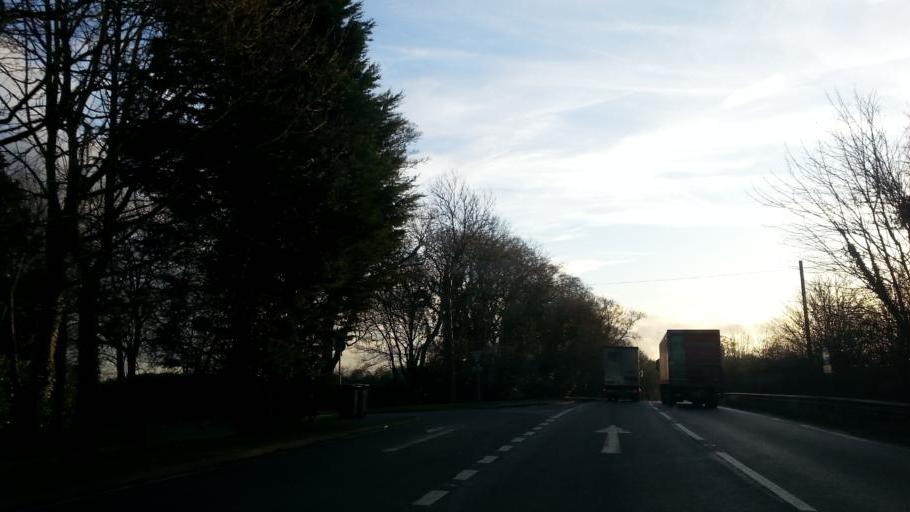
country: GB
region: England
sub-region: Northamptonshire
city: Brackley
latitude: 52.0174
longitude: -1.1520
